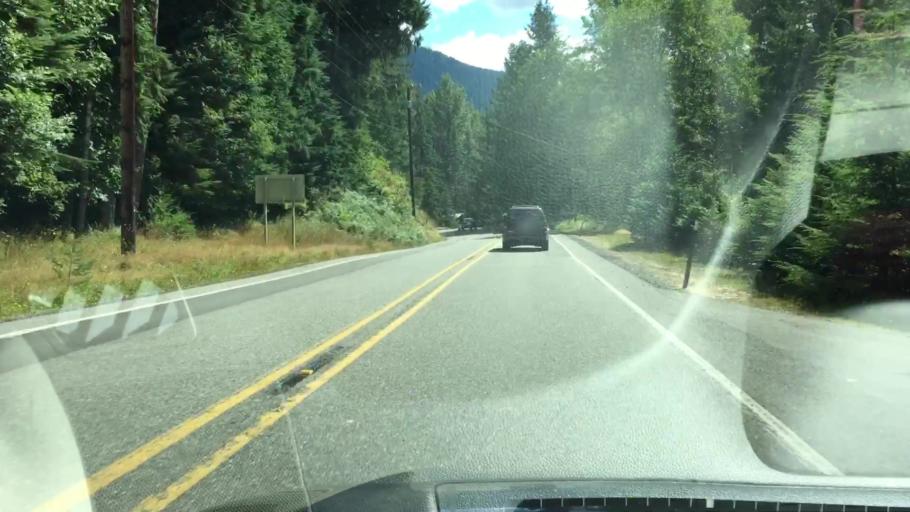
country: US
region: Washington
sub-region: Pierce County
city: Eatonville
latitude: 46.7449
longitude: -121.9237
